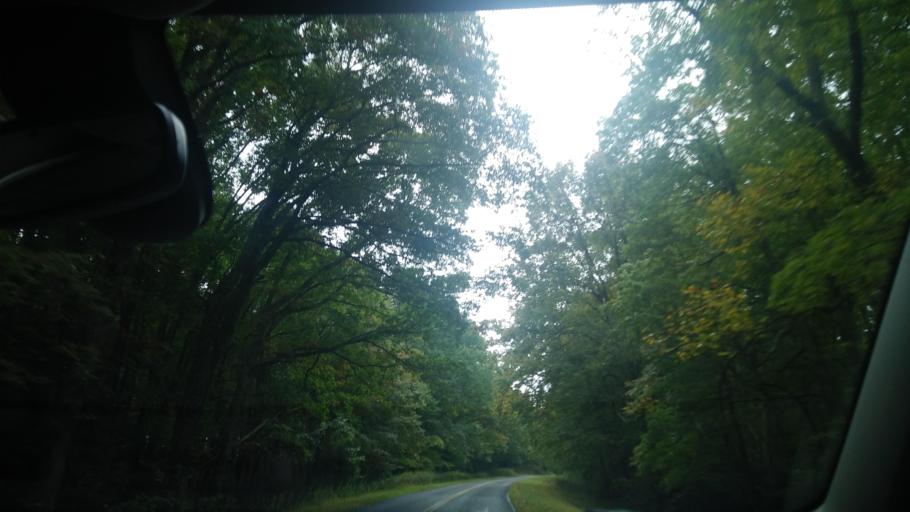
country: US
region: Virginia
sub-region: Carroll County
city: Cana
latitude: 36.6486
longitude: -80.5508
